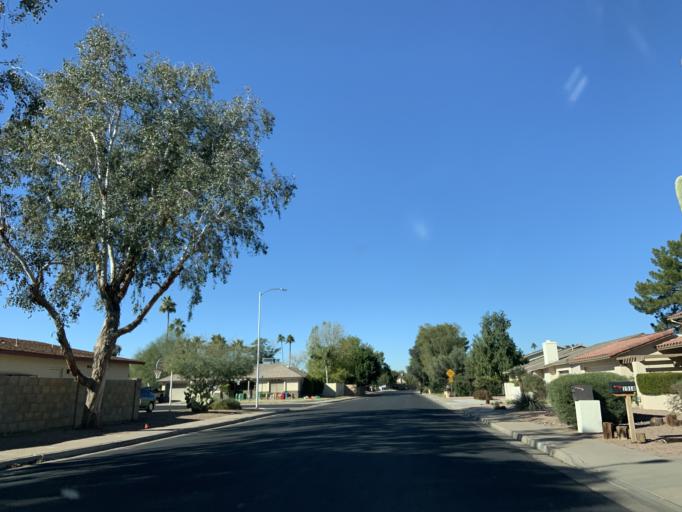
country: US
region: Arizona
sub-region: Maricopa County
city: San Carlos
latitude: 33.3669
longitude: -111.8664
